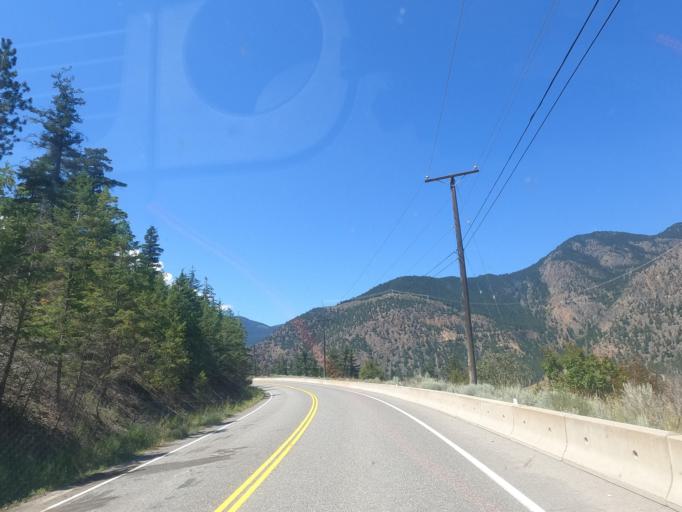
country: CA
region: British Columbia
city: Lillooet
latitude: 50.7588
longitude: -121.9090
